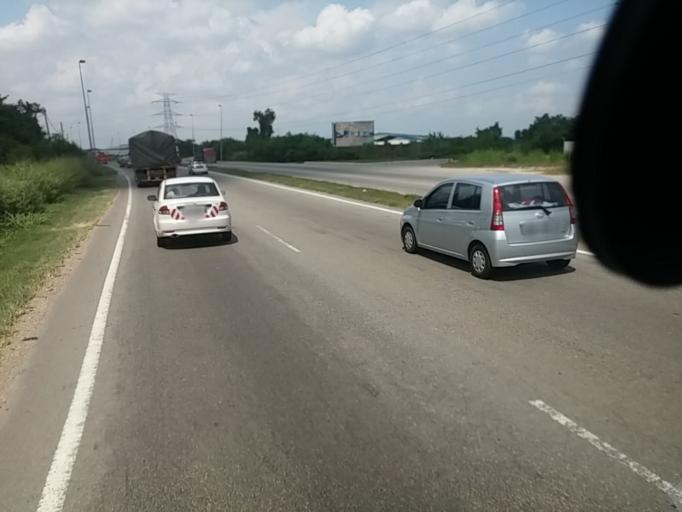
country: MY
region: Selangor
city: Klang
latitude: 2.9779
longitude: 101.3936
